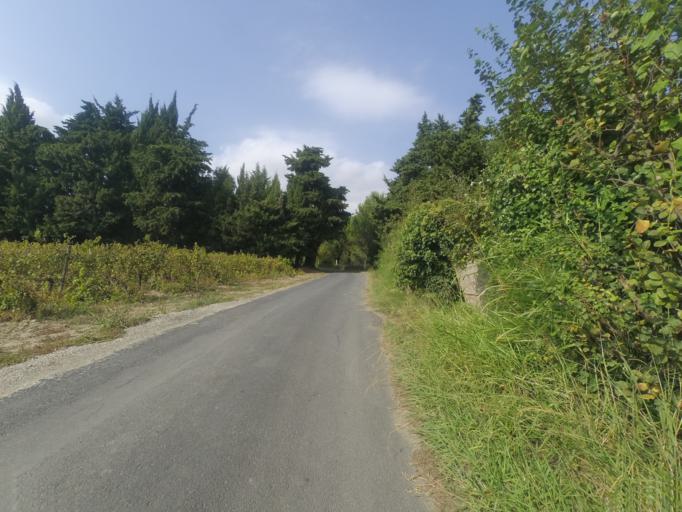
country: FR
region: Languedoc-Roussillon
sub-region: Departement des Pyrenees-Orientales
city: Pezilla-la-Riviere
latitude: 42.6894
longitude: 2.7772
